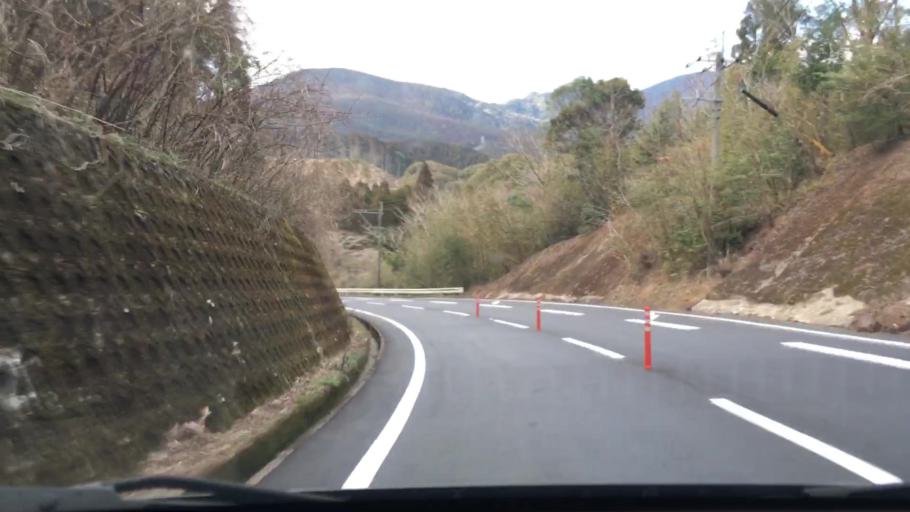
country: JP
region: Miyazaki
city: Nichinan
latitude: 31.7059
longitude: 131.3301
